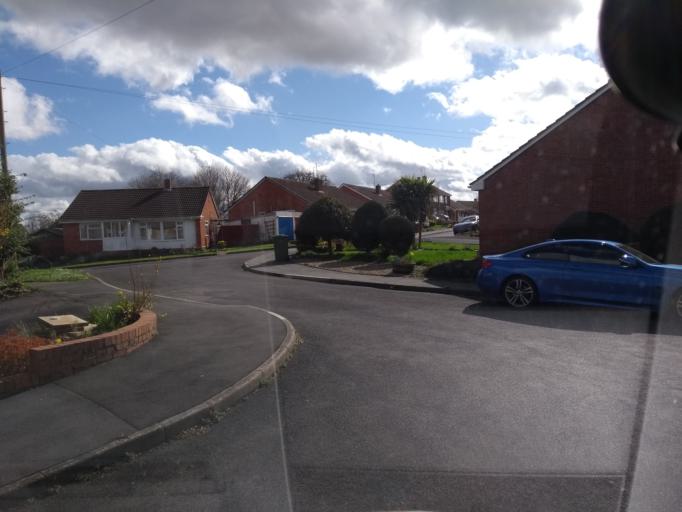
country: GB
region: England
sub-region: Somerset
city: Creech Saint Michael
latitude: 51.0306
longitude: -3.0413
